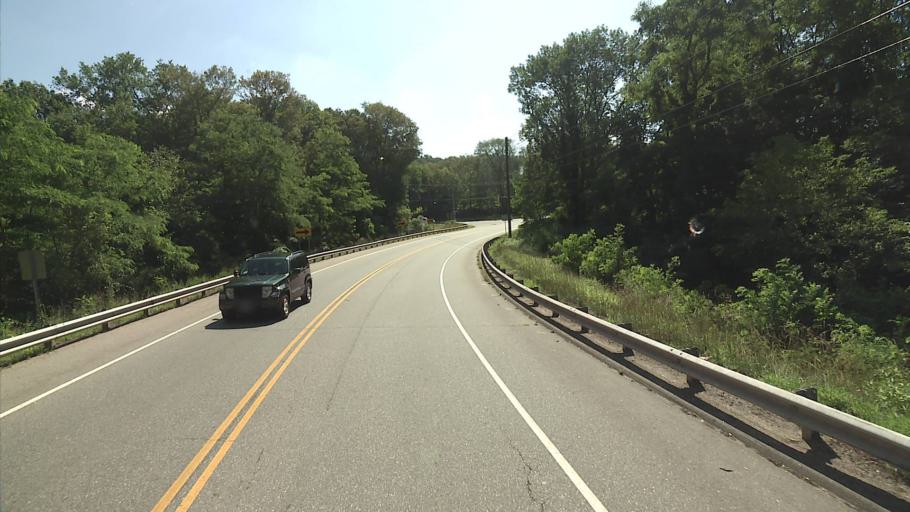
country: US
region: Connecticut
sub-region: Windham County
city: Windham
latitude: 41.7101
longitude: -72.1671
